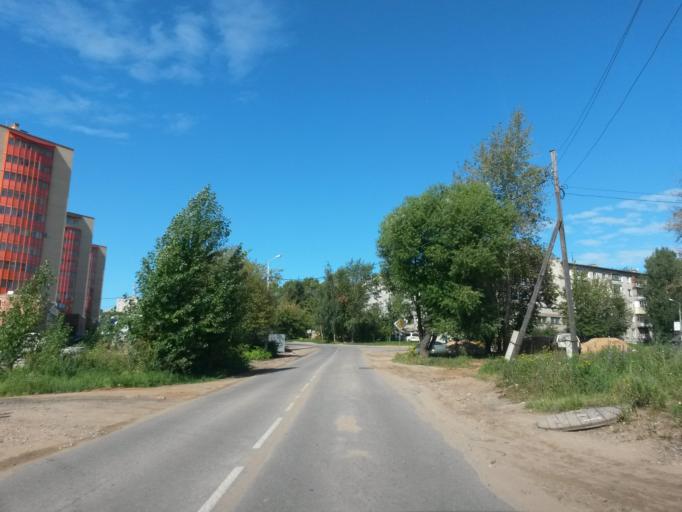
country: RU
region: Jaroslavl
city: Yaroslavl
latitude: 57.5774
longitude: 39.8664
